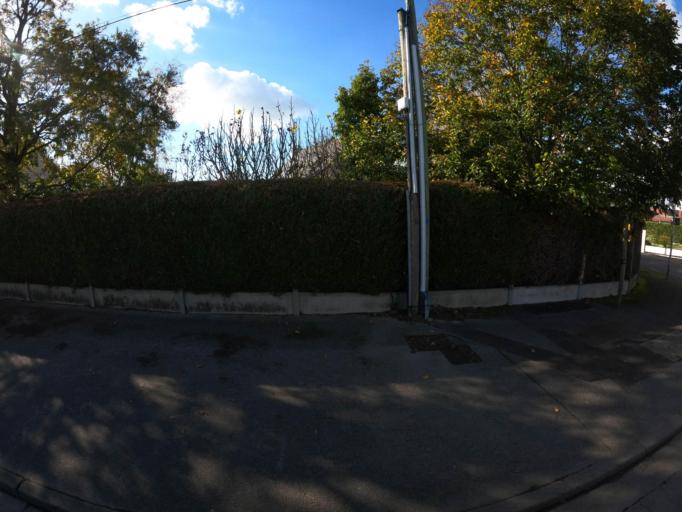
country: FR
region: Pays de la Loire
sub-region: Departement de la Loire-Atlantique
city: La Baule-Escoublac
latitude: 47.2924
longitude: -2.3572
